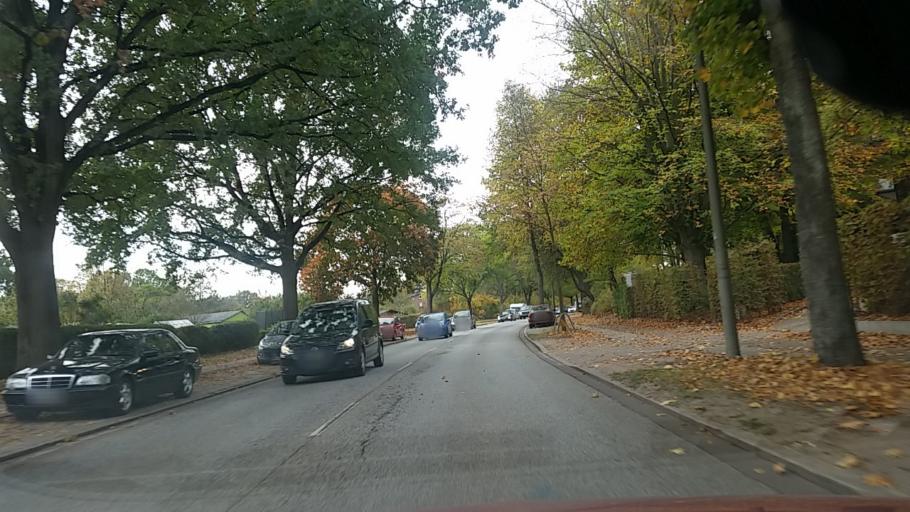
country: DE
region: Hamburg
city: Ohlsdorf
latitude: 53.6192
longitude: 10.0226
